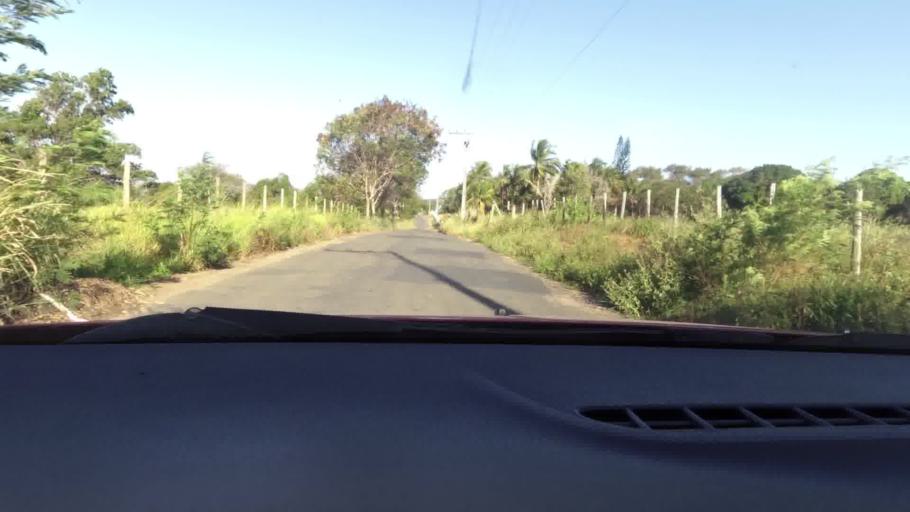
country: BR
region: Espirito Santo
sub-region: Guarapari
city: Guarapari
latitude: -20.5318
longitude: -40.4576
